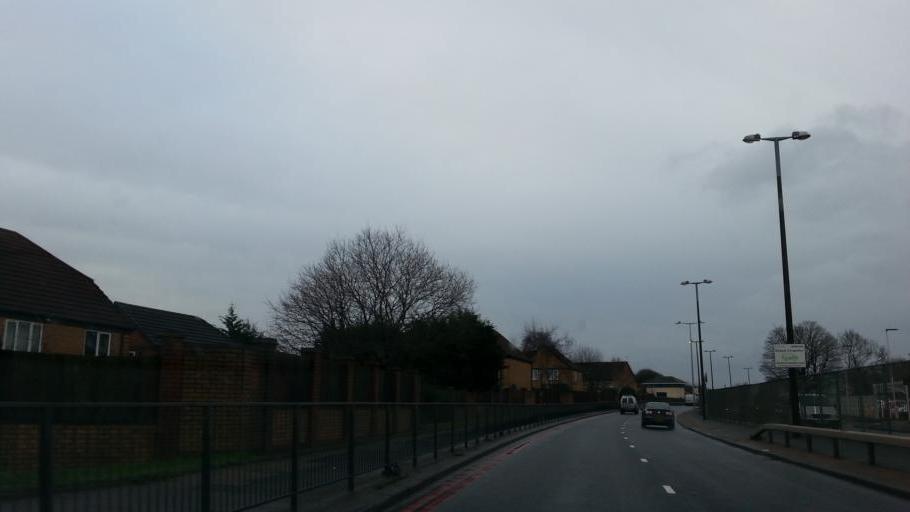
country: GB
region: England
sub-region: Sandwell
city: Smethwick
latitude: 52.5023
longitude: -1.9837
